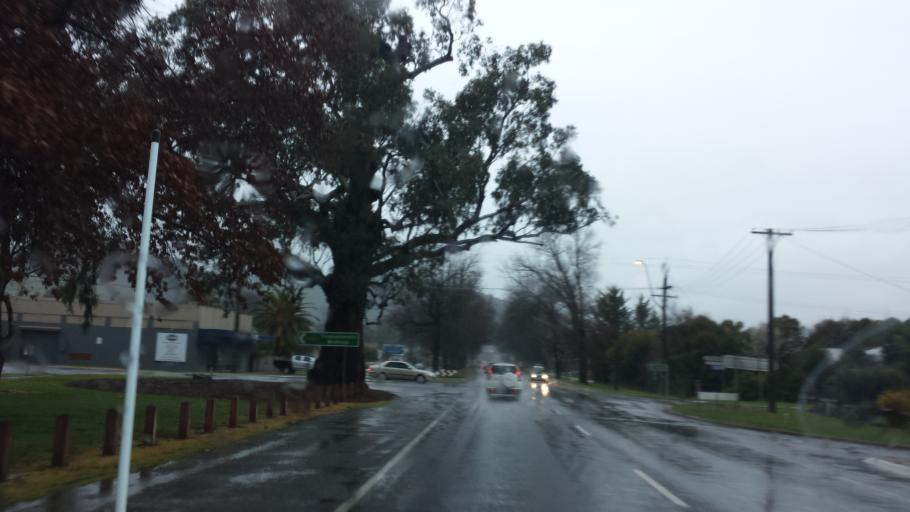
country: AU
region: Victoria
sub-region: Wangaratta
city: Wangaratta
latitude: -36.5580
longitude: 146.7193
